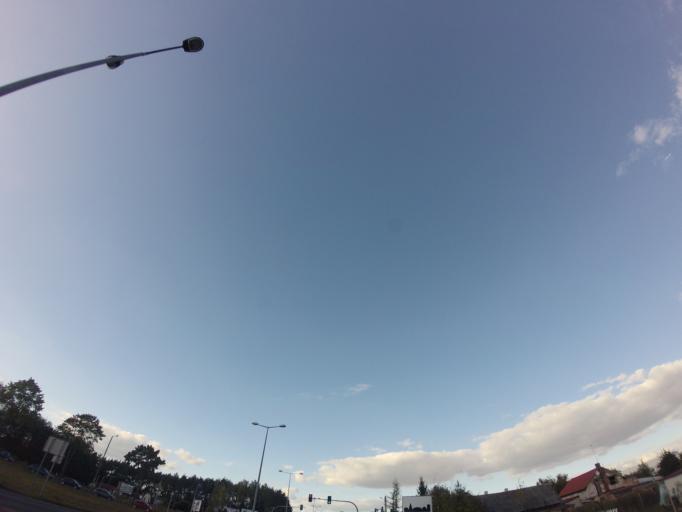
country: PL
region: Greater Poland Voivodeship
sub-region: Powiat nowotomyski
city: Nowy Tomysl
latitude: 52.3123
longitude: 16.1107
